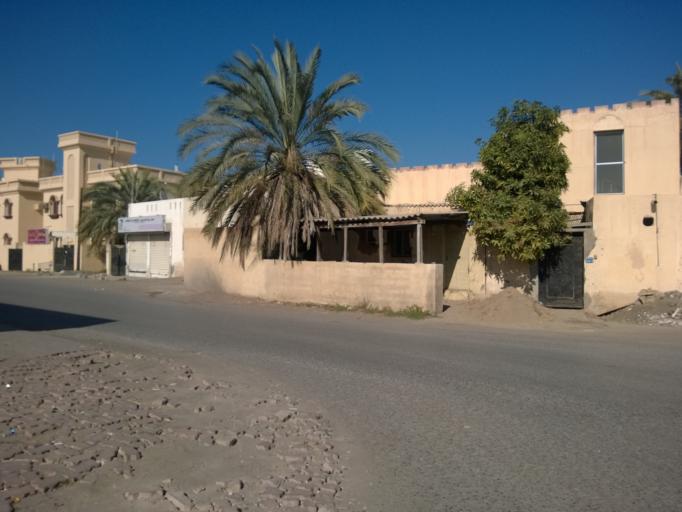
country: OM
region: Muhafazat Masqat
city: As Sib al Jadidah
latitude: 23.6818
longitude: 58.1874
